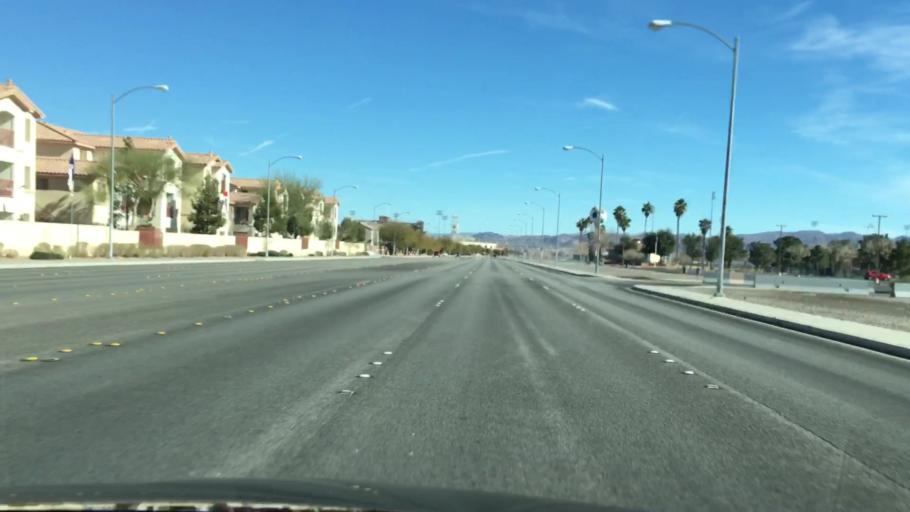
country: US
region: Nevada
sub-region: Clark County
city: Whitney
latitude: 36.0855
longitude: -115.0273
